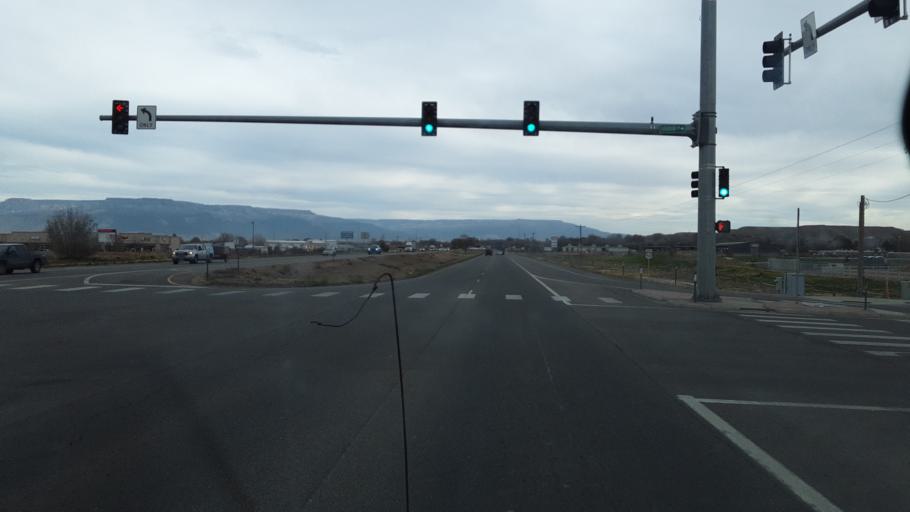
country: US
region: Colorado
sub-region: Mesa County
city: Orchard Mesa
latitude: 39.0383
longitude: -108.5388
